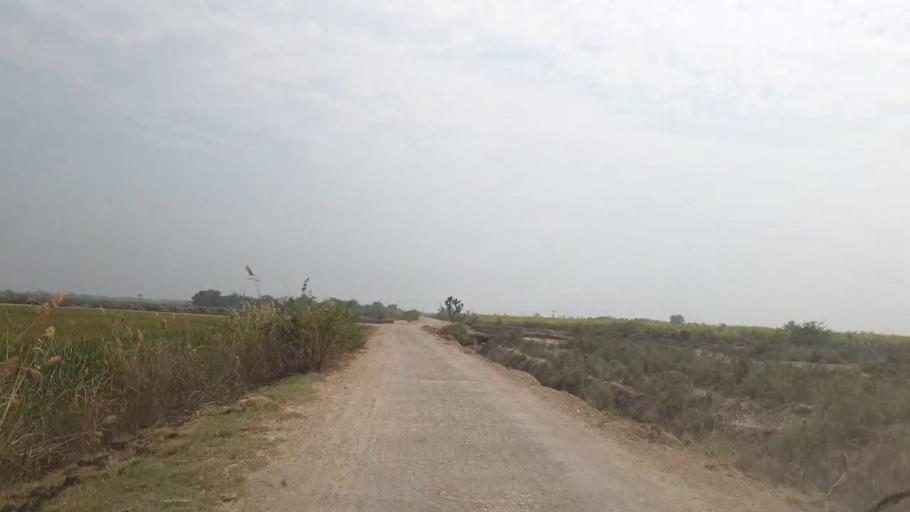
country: PK
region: Sindh
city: Mirpur Khas
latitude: 25.5405
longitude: 69.1280
